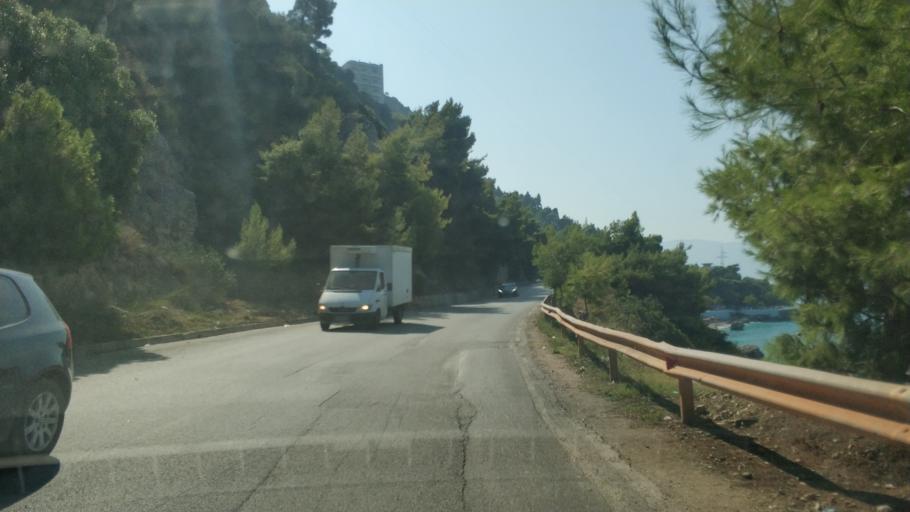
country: AL
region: Vlore
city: Vlore
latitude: 40.4090
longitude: 19.4805
